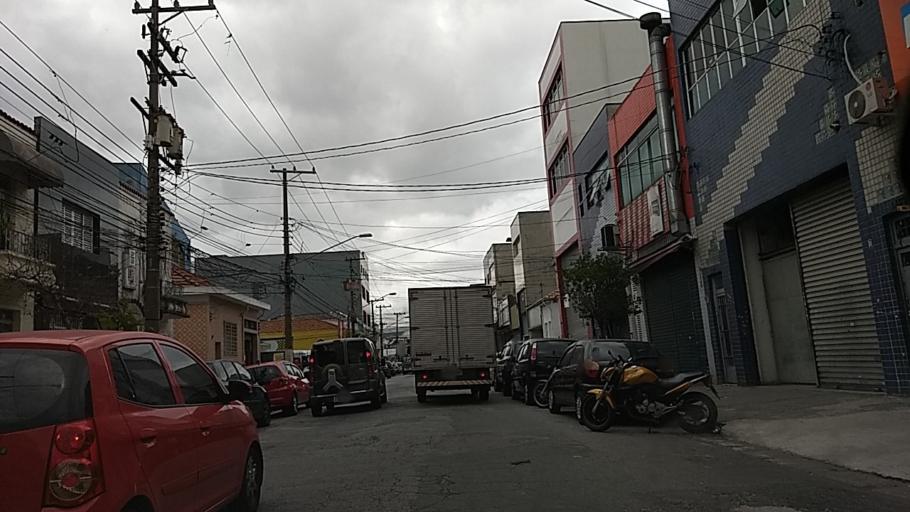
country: BR
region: Sao Paulo
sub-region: Sao Paulo
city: Sao Paulo
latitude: -23.5291
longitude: -46.6168
